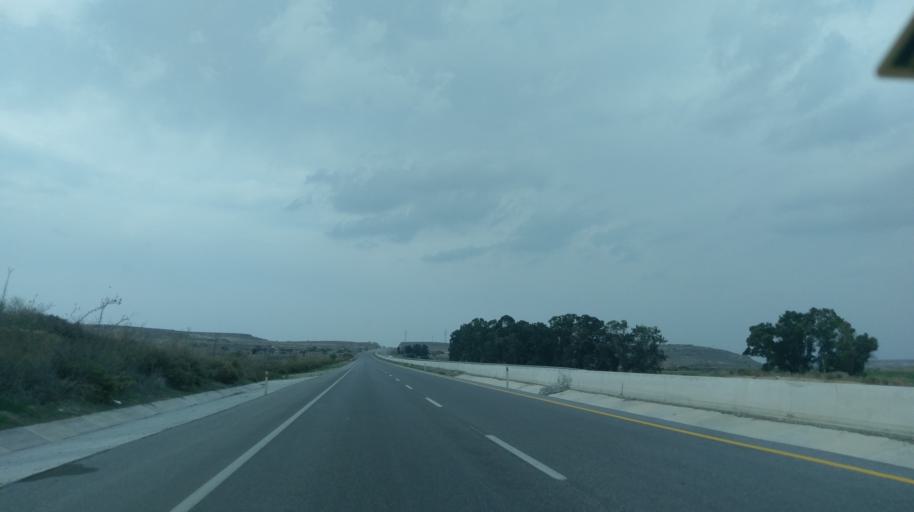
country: CY
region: Lefkosia
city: Peristerona
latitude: 35.1957
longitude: 33.0875
